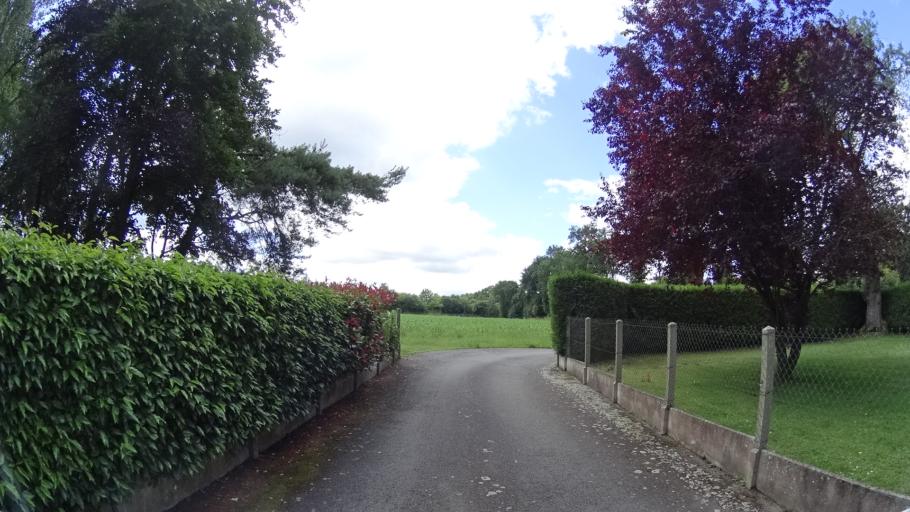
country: FR
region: Brittany
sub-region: Departement d'Ille-et-Vilaine
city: Saint-Gilles
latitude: 48.1312
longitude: -1.8236
